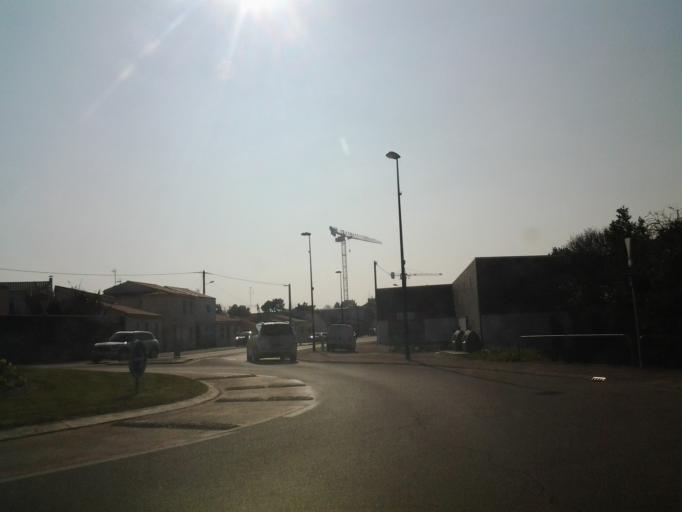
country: FR
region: Pays de la Loire
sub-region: Departement de la Vendee
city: Les Sables-d'Olonne
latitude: 46.5066
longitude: -1.7709
